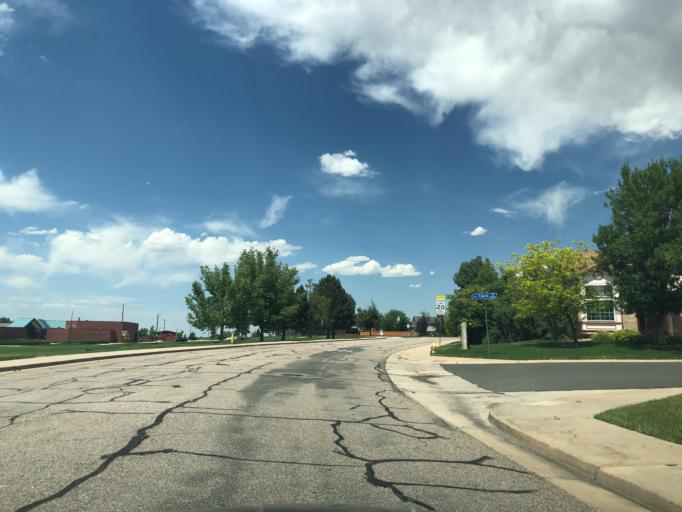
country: US
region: Colorado
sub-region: Arapahoe County
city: Dove Valley
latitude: 39.6210
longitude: -104.7618
